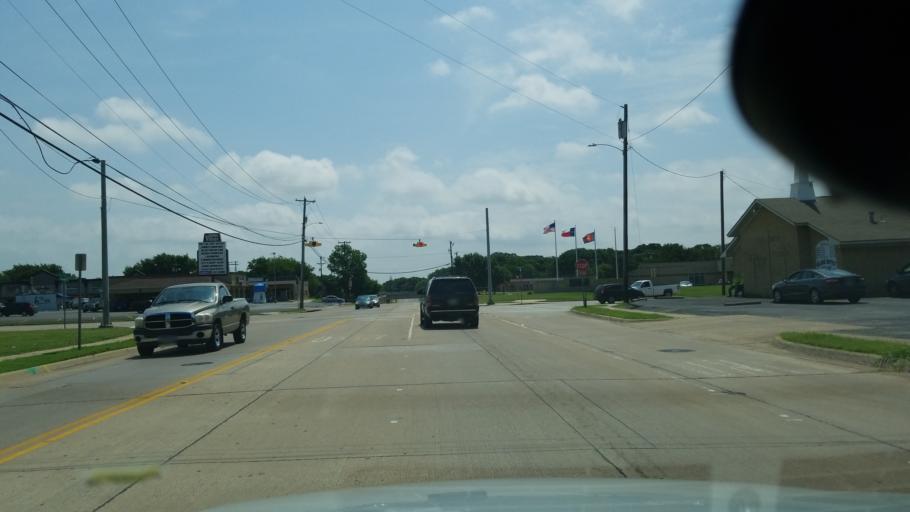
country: US
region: Texas
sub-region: Dallas County
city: Irving
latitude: 32.8293
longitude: -96.9448
